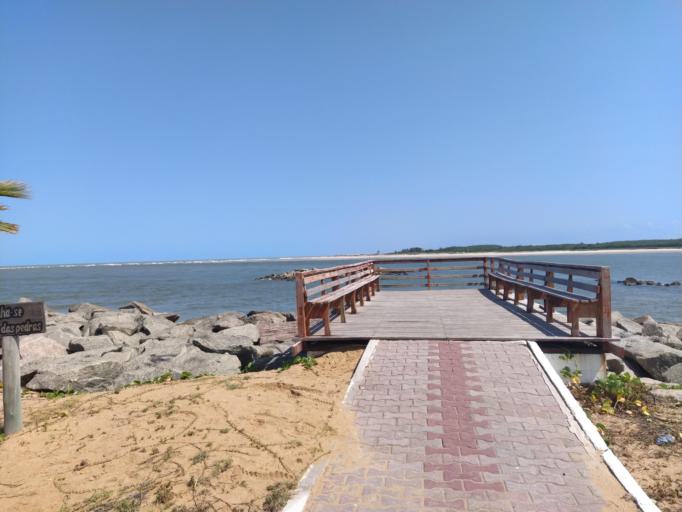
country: BR
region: Espirito Santo
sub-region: Conceicao Da Barra
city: Conceicao da Barra
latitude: -18.6001
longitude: -39.7281
